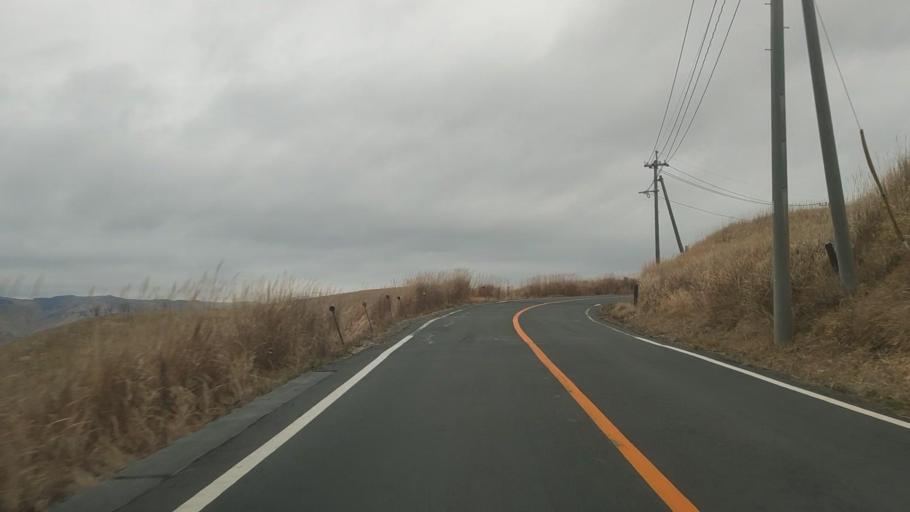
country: JP
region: Kumamoto
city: Aso
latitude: 32.9021
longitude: 131.0297
